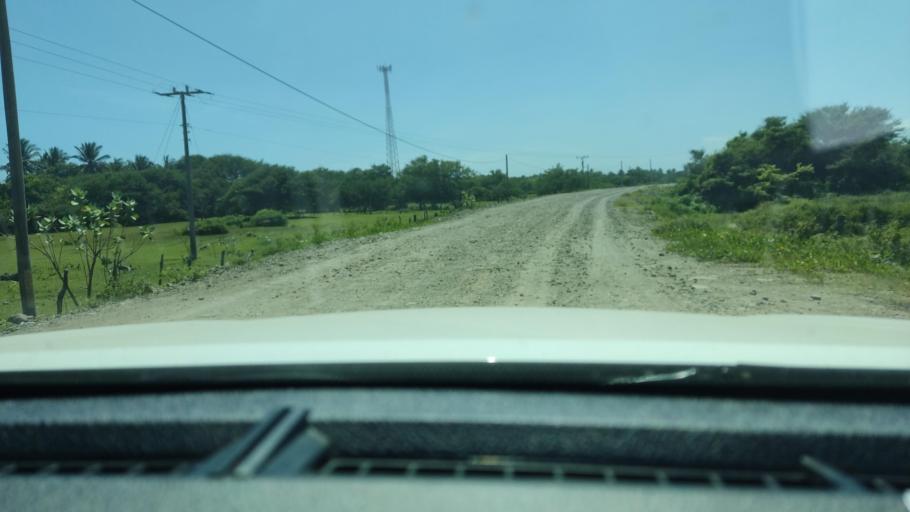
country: SV
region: Ahuachapan
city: San Francisco Menendez
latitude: 13.7679
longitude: -90.1798
